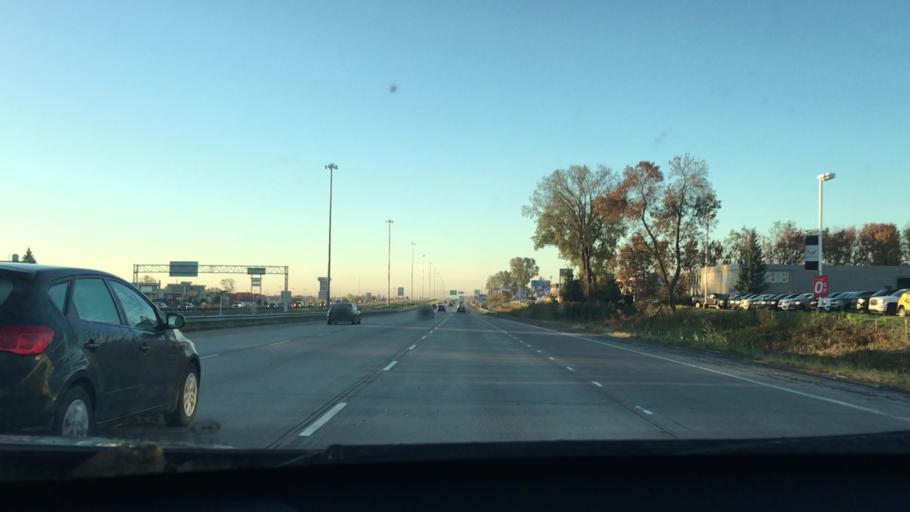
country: CA
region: Quebec
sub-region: Laurentides
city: Saint-Jerome
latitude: 45.7736
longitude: -74.0209
